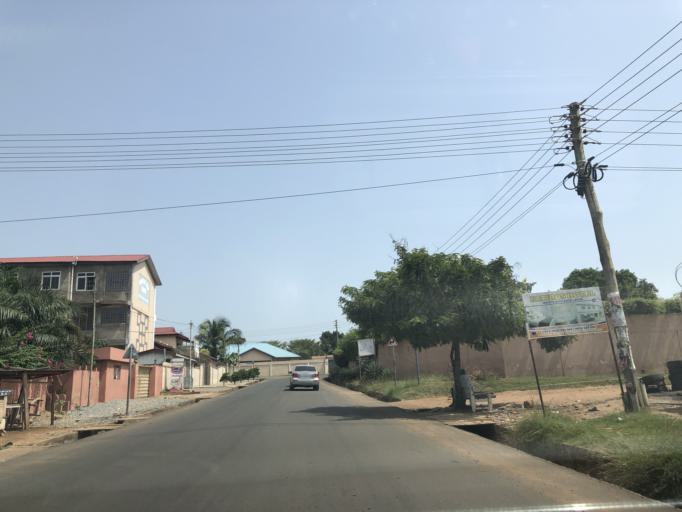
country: GH
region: Greater Accra
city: Dome
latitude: 5.6199
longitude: -0.2502
